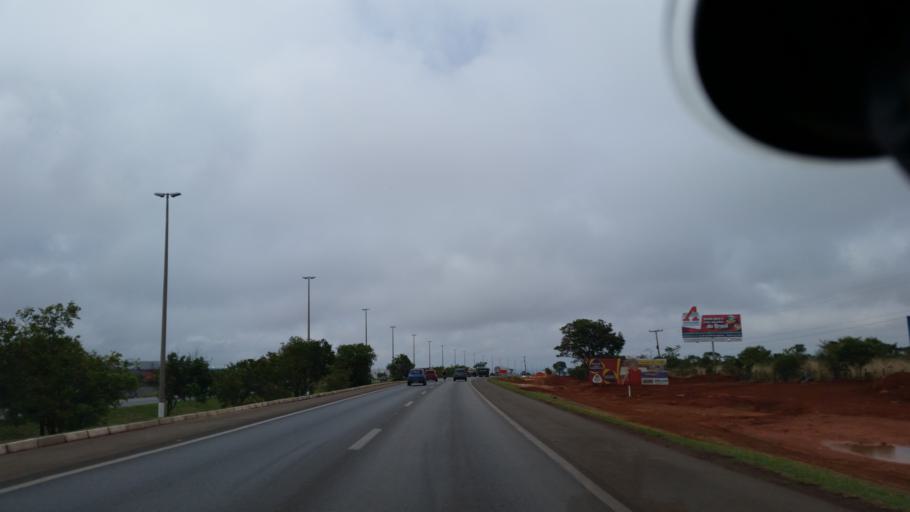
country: BR
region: Goias
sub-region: Luziania
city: Luziania
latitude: -16.0298
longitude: -47.9789
